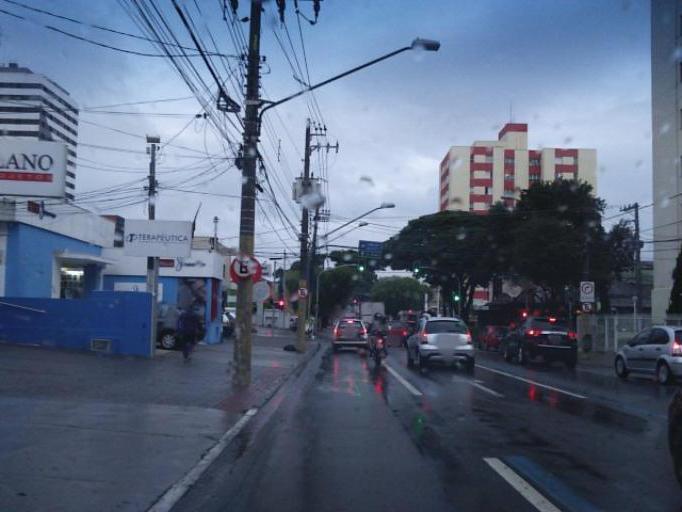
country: BR
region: Sao Paulo
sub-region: Sao Jose Dos Campos
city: Sao Jose dos Campos
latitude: -23.2022
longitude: -45.8930
